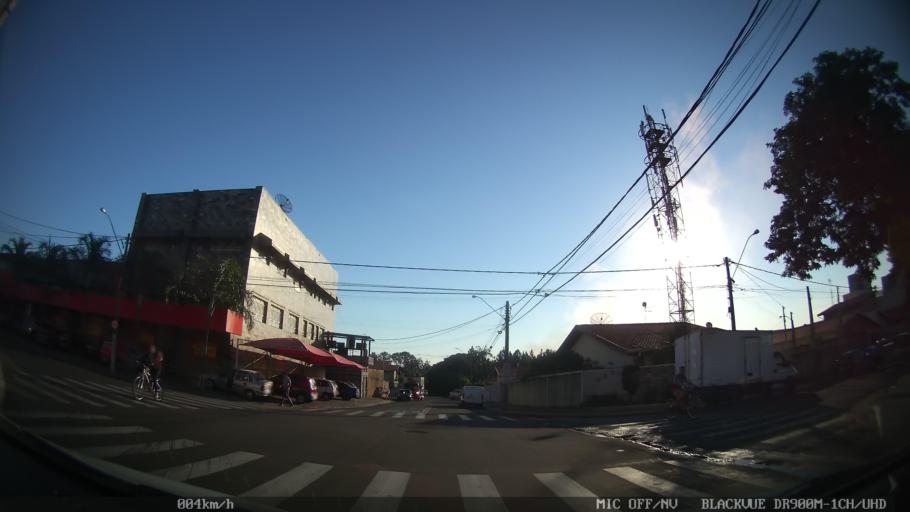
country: BR
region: Sao Paulo
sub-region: Nova Odessa
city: Nova Odessa
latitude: -22.7787
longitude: -47.2835
